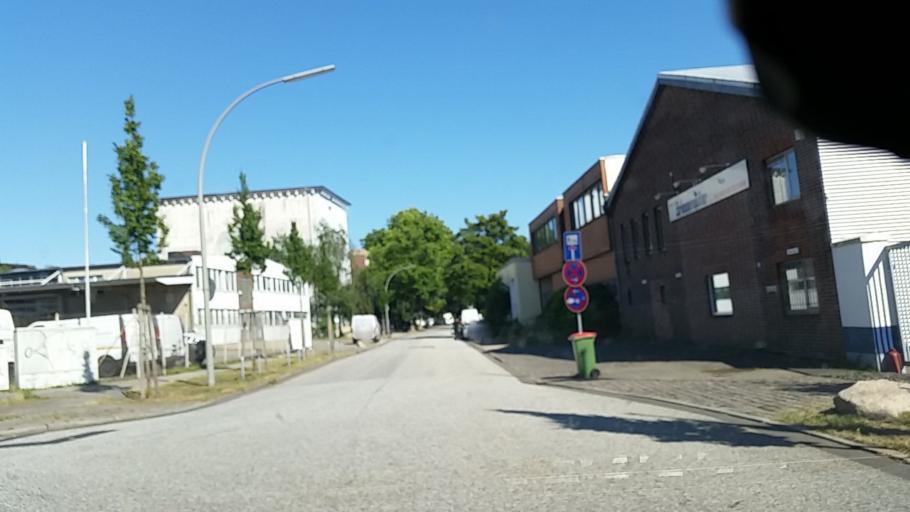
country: DE
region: Hamburg
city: Rothenburgsort
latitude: 53.5454
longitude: 10.0487
